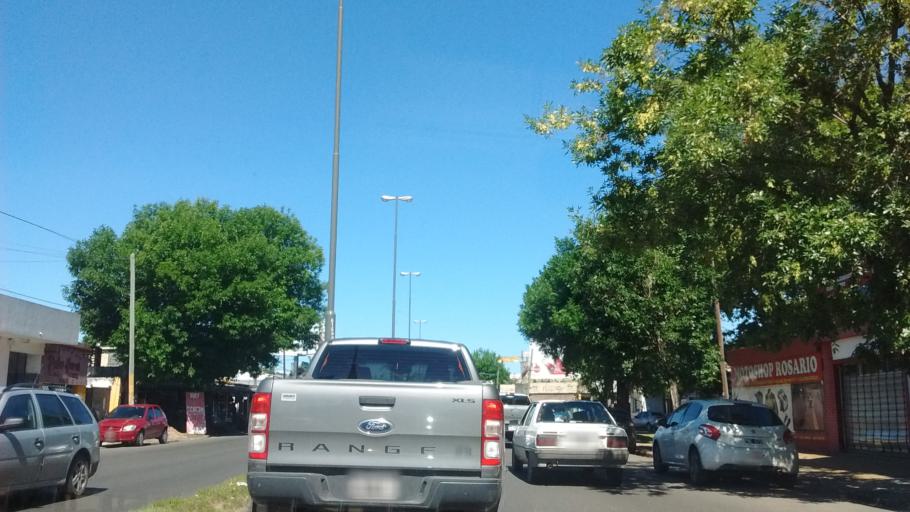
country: AR
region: Santa Fe
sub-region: Departamento de Rosario
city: Rosario
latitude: -32.9341
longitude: -60.7069
